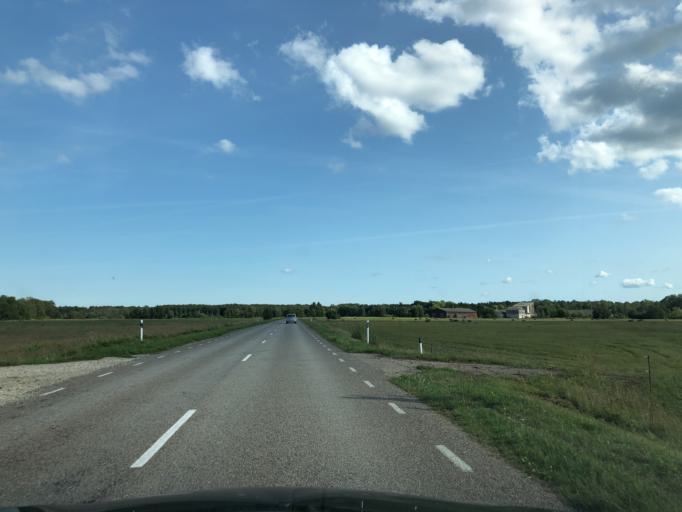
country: EE
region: Hiiumaa
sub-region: Kaerdla linn
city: Kardla
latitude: 58.7134
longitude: 22.5792
